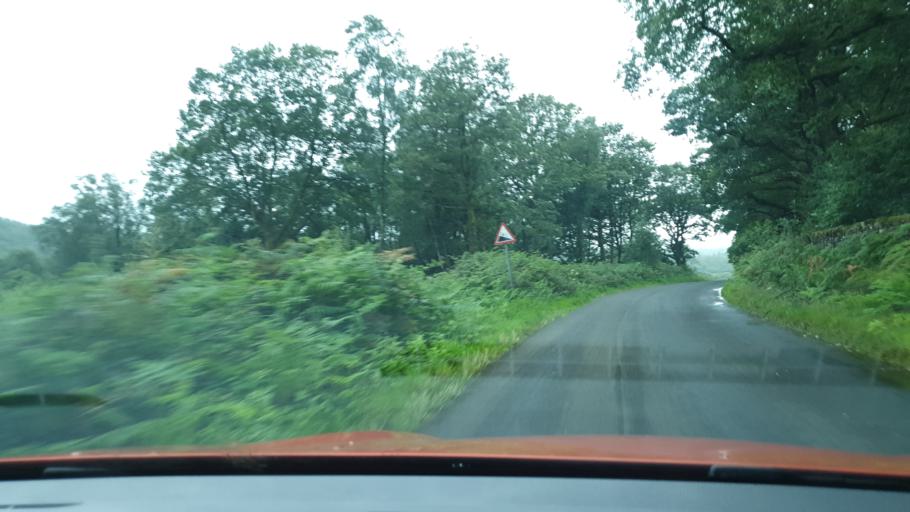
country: GB
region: England
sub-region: Cumbria
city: Seascale
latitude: 54.4089
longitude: -3.3660
